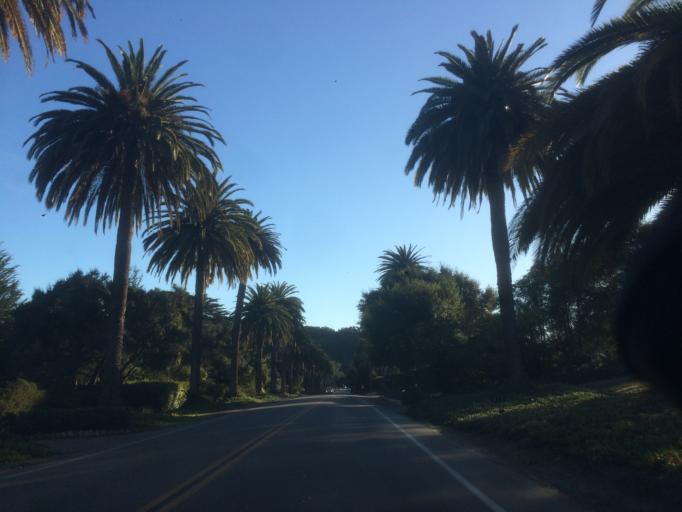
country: US
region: California
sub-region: Santa Barbara County
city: Mission Canyon
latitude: 34.4285
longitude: -119.7632
